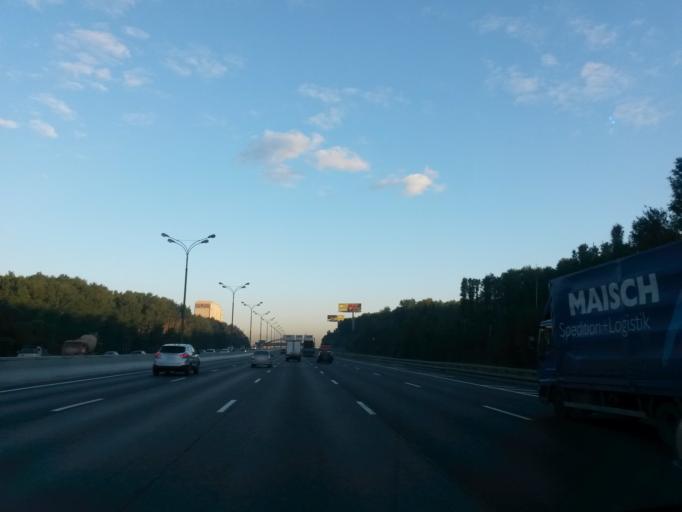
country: RU
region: Moskovskaya
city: Druzhba
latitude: 55.8742
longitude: 37.7423
